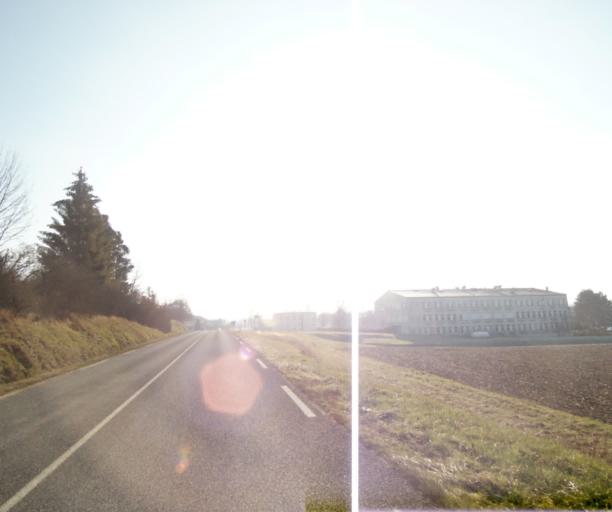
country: FR
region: Champagne-Ardenne
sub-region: Departement de la Haute-Marne
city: Wassy
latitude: 48.5068
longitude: 4.9417
